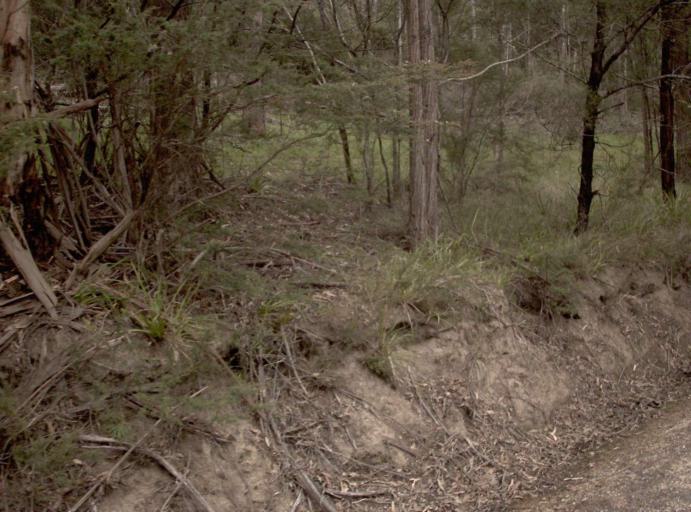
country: AU
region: New South Wales
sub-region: Bombala
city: Bombala
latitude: -37.4096
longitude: 149.1976
